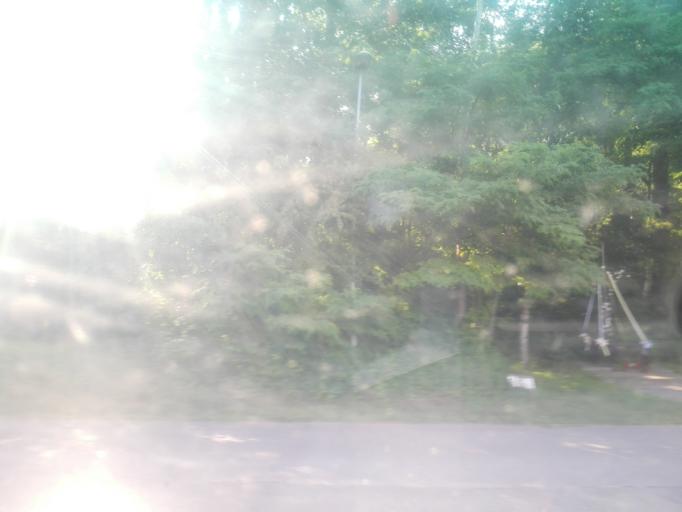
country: PL
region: Silesian Voivodeship
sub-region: Powiat czestochowski
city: Mstow
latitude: 50.8389
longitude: 19.3263
